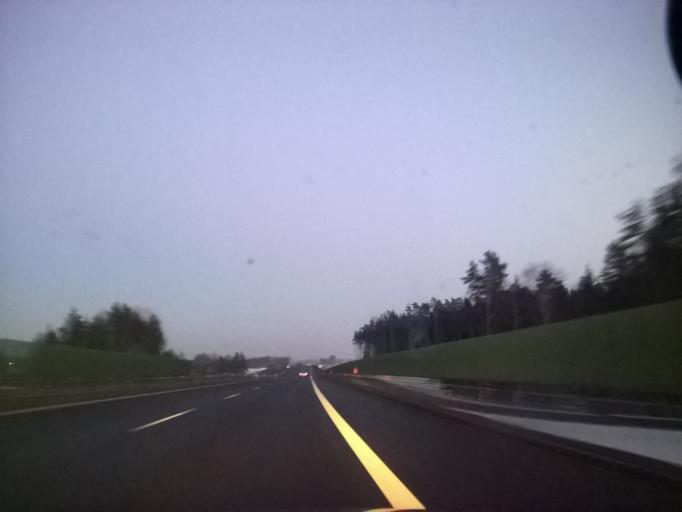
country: PL
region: Warmian-Masurian Voivodeship
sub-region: Powiat olsztynski
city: Biskupiec
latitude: 53.8461
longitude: 20.9854
